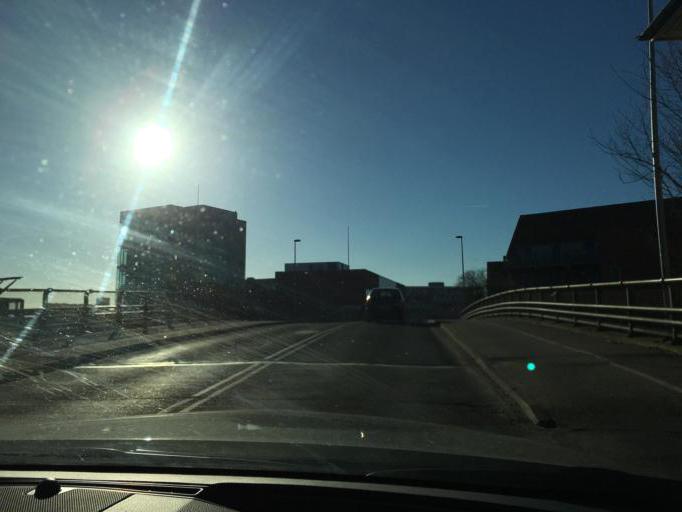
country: DK
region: South Denmark
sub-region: Kolding Kommune
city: Kolding
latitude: 55.4895
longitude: 9.4788
